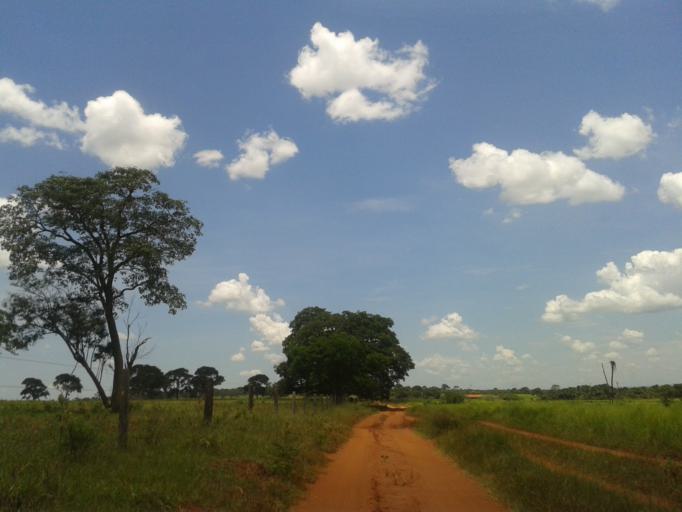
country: BR
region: Minas Gerais
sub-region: Santa Vitoria
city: Santa Vitoria
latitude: -19.2131
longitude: -50.4107
